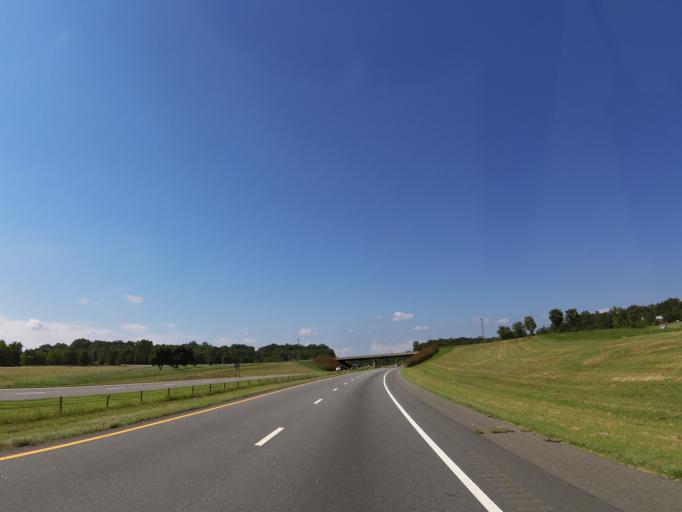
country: US
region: North Carolina
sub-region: Catawba County
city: Mountain View
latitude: 35.6772
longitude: -81.3389
